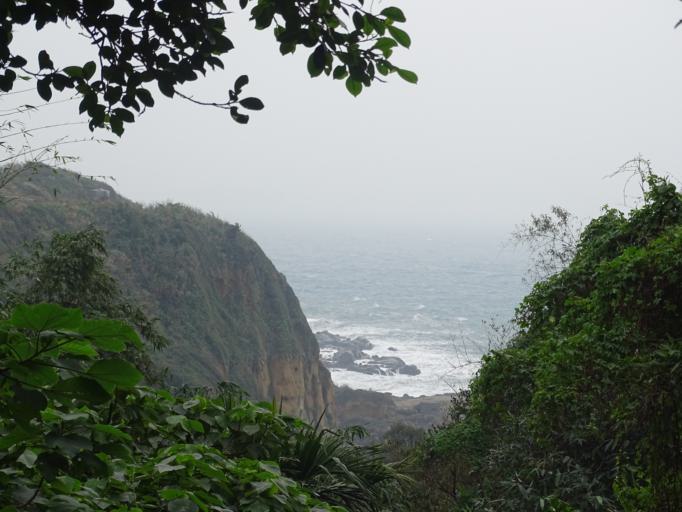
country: TW
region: Taiwan
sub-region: Keelung
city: Keelung
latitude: 25.1582
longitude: 121.7721
